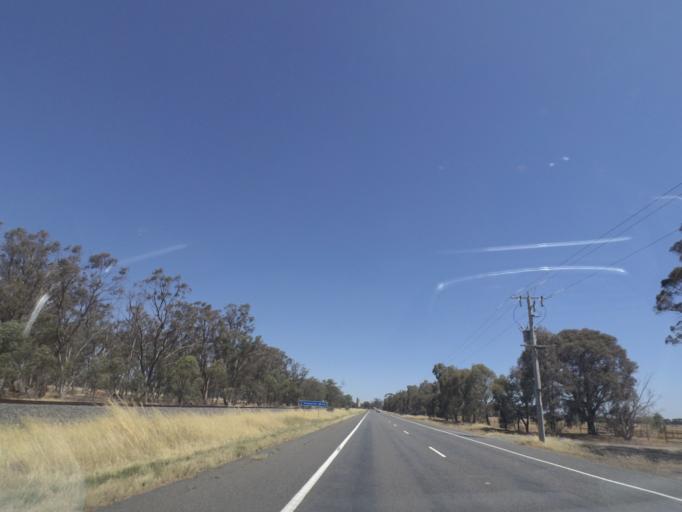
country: AU
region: Victoria
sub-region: Greater Shepparton
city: Shepparton
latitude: -36.2286
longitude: 145.4318
